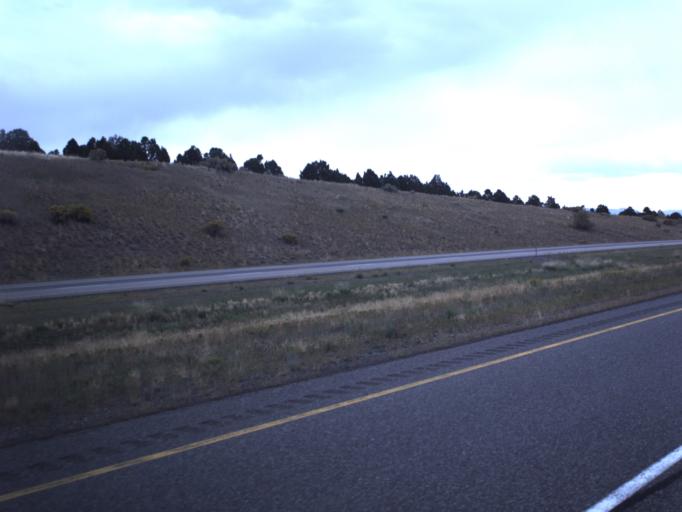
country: US
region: Utah
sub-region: Sevier County
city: Monroe
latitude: 38.5535
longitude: -112.4137
